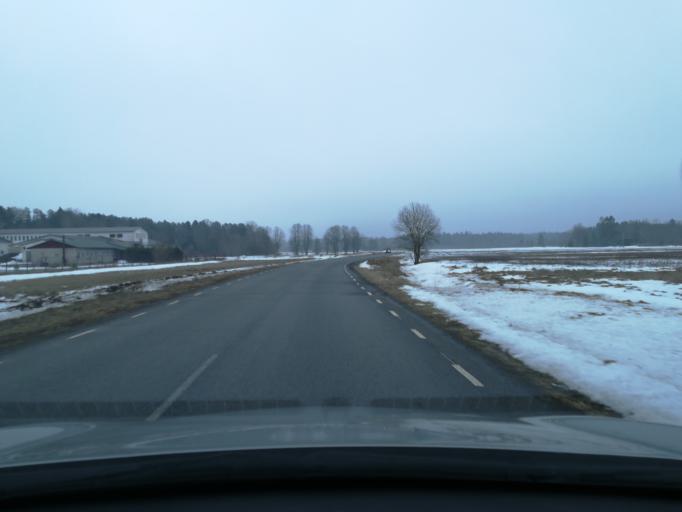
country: EE
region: Harju
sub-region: Kuusalu vald
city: Kuusalu
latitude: 59.4713
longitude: 25.5648
